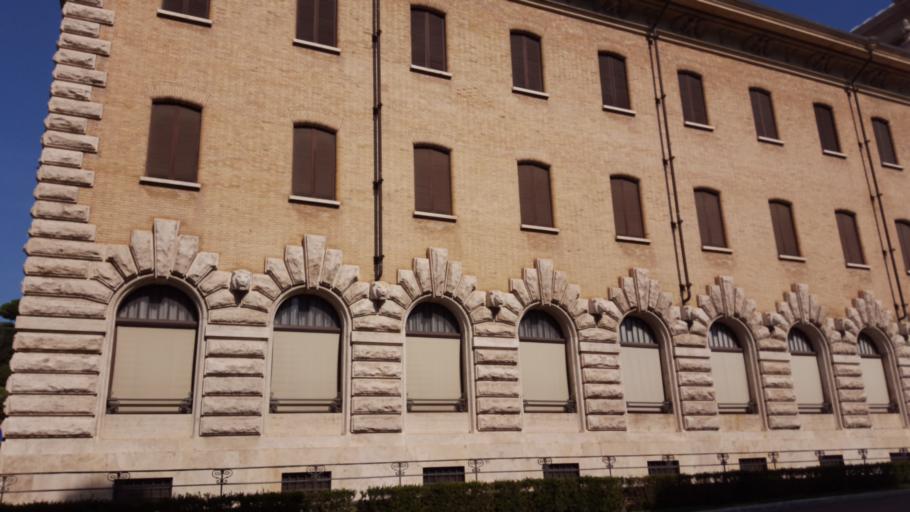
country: VA
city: Vatican City
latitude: 41.9019
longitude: 12.4513
